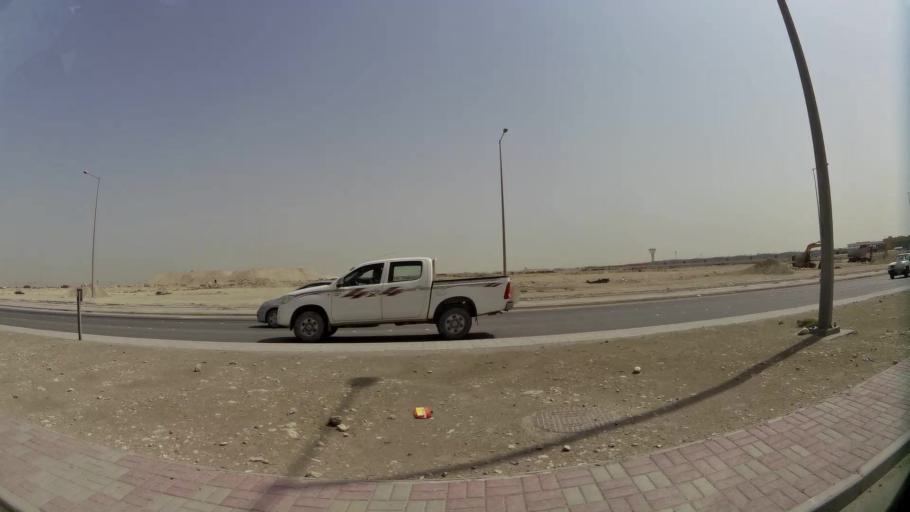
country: QA
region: Baladiyat ar Rayyan
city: Ar Rayyan
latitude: 25.1704
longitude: 51.4007
